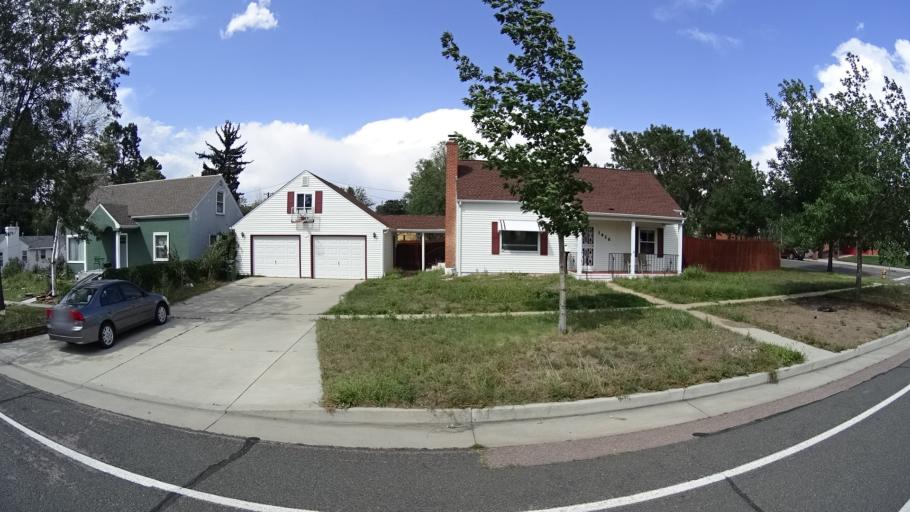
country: US
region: Colorado
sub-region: El Paso County
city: Colorado Springs
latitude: 38.8458
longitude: -104.7989
